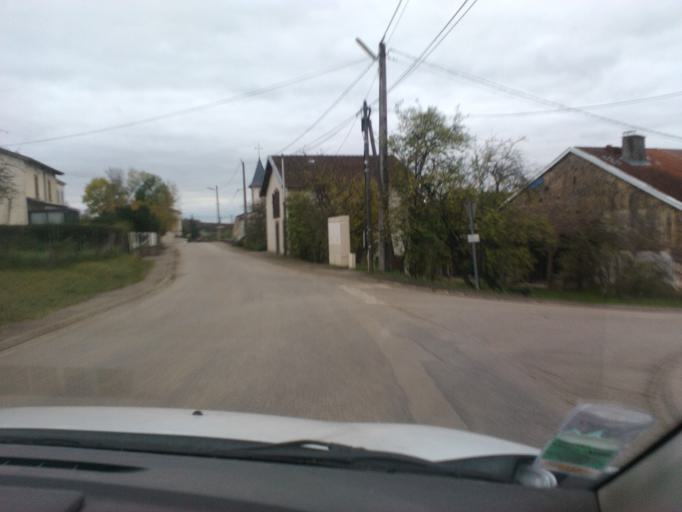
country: FR
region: Lorraine
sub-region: Departement des Vosges
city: Mirecourt
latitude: 48.2859
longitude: 6.1932
